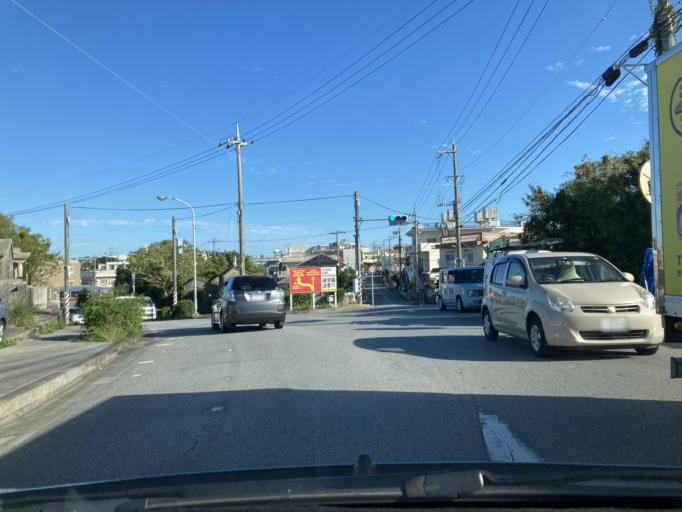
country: JP
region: Okinawa
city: Chatan
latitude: 26.3609
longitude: 127.7493
